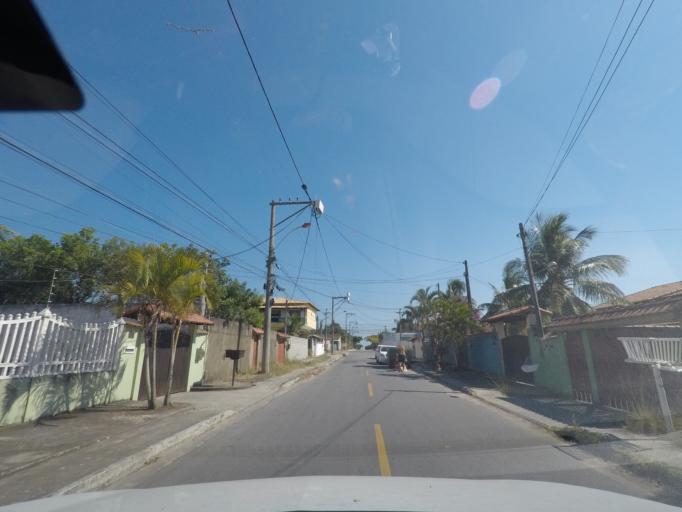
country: BR
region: Rio de Janeiro
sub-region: Niteroi
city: Niteroi
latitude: -22.9640
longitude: -42.9720
